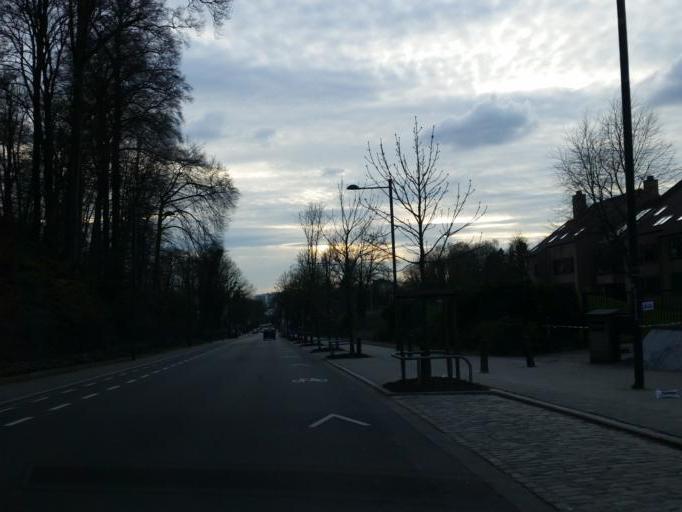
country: BE
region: Flanders
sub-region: Provincie Vlaams-Brabant
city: Linkebeek
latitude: 50.8042
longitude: 4.3517
